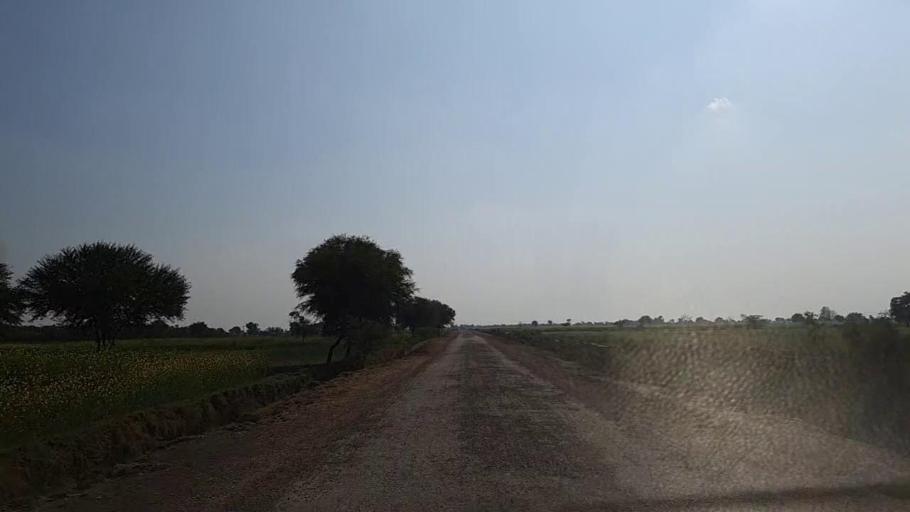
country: PK
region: Sindh
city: Jam Sahib
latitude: 26.2592
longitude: 68.5670
